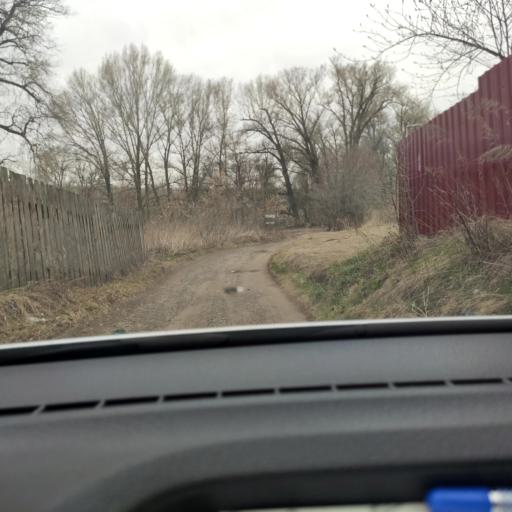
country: RU
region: Bashkortostan
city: Avdon
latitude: 54.5997
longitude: 55.6123
